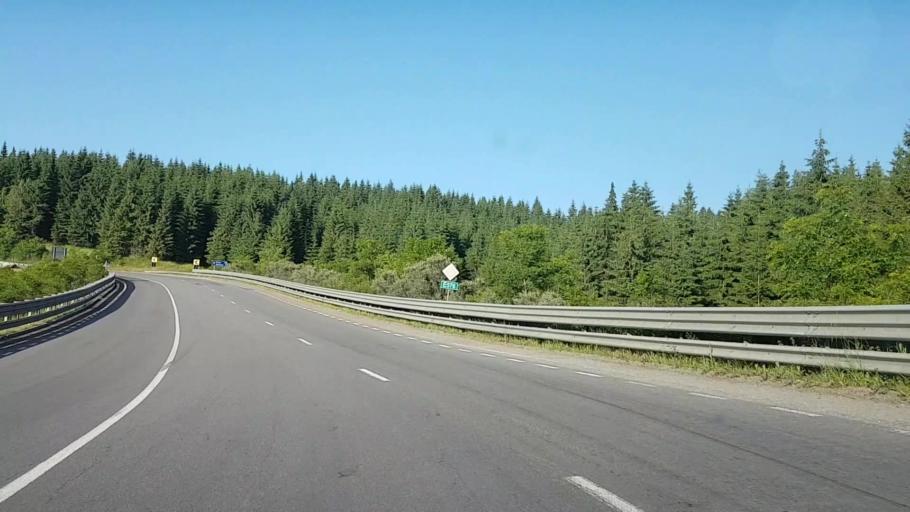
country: RO
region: Bistrita-Nasaud
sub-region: Comuna Lunca Ilvei
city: Lunca Ilvei
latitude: 47.2399
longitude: 25.0176
